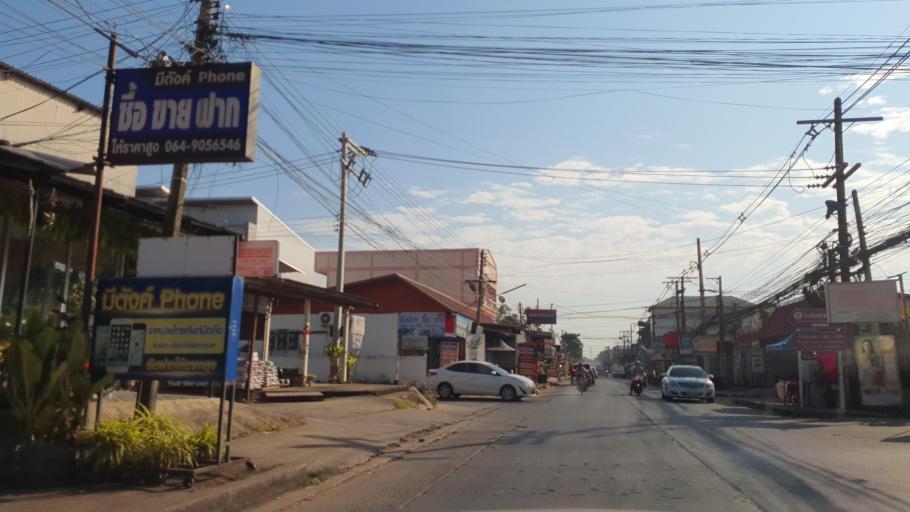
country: TH
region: Khon Kaen
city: Khon Kaen
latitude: 16.4214
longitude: 102.8117
